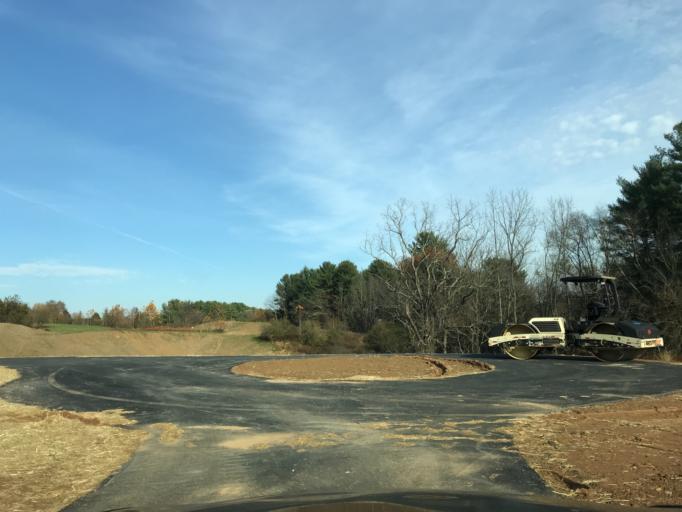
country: US
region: Maryland
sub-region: Baltimore County
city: Reisterstown
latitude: 39.4942
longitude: -76.9089
